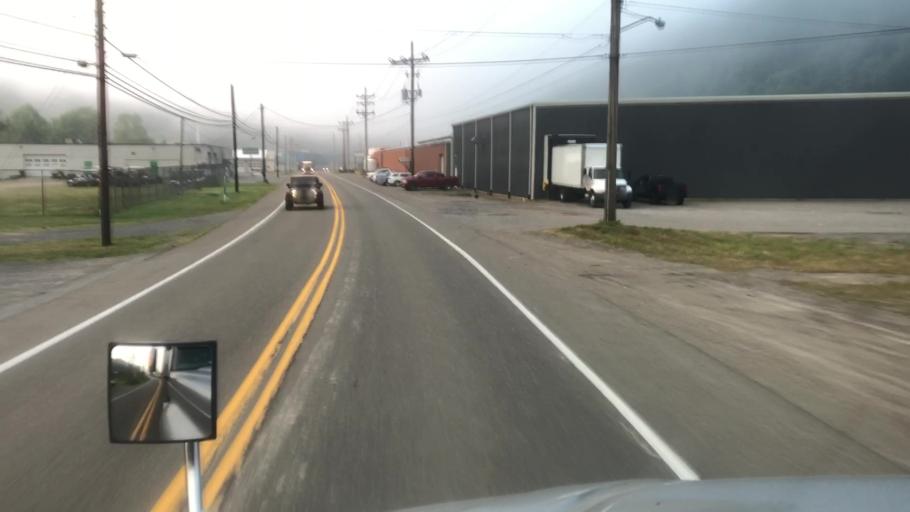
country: US
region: Pennsylvania
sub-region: Venango County
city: Hasson Heights
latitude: 41.4585
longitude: -79.6902
